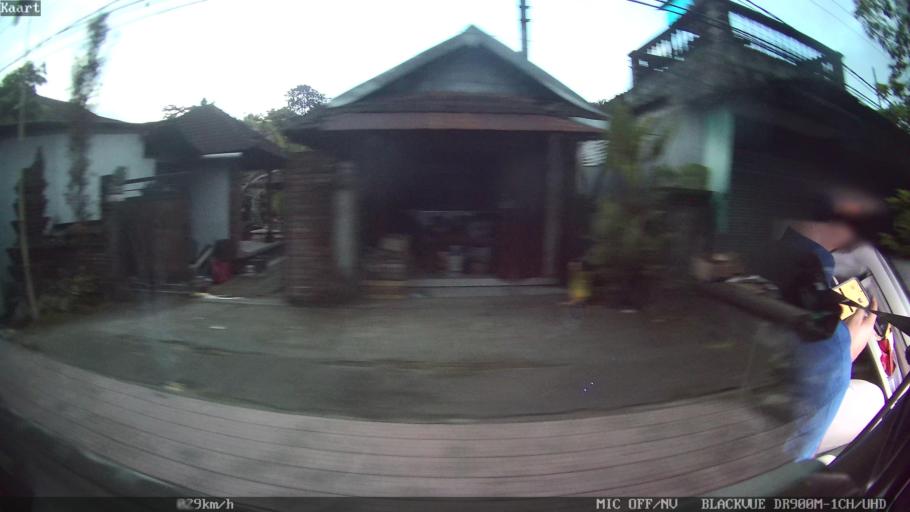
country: ID
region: Bali
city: Bunutan
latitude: -8.4789
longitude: 115.2481
